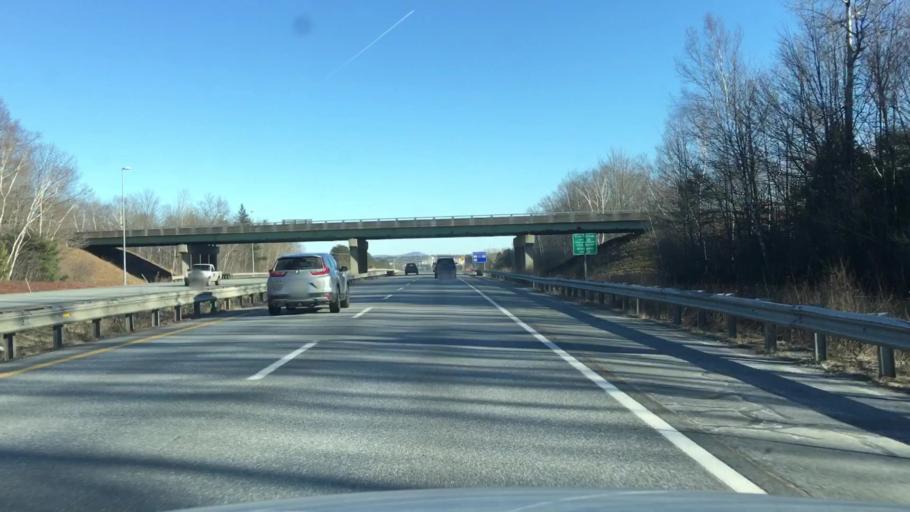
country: US
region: Maine
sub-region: Penobscot County
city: Bangor
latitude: 44.7865
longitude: -68.7954
